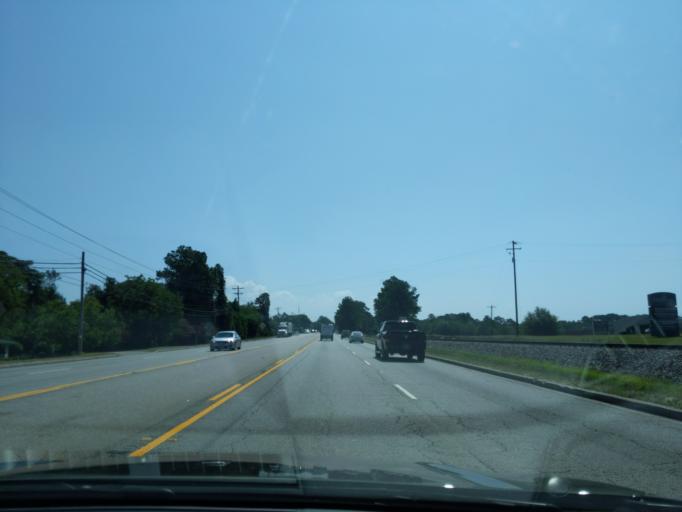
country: US
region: South Carolina
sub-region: Lexington County
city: Oak Grove
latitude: 33.9750
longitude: -81.1699
